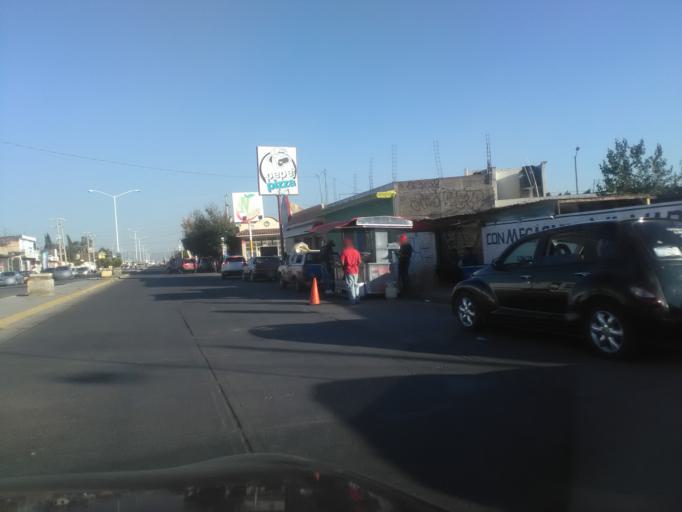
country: MX
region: Durango
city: Victoria de Durango
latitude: 24.0598
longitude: -104.5932
